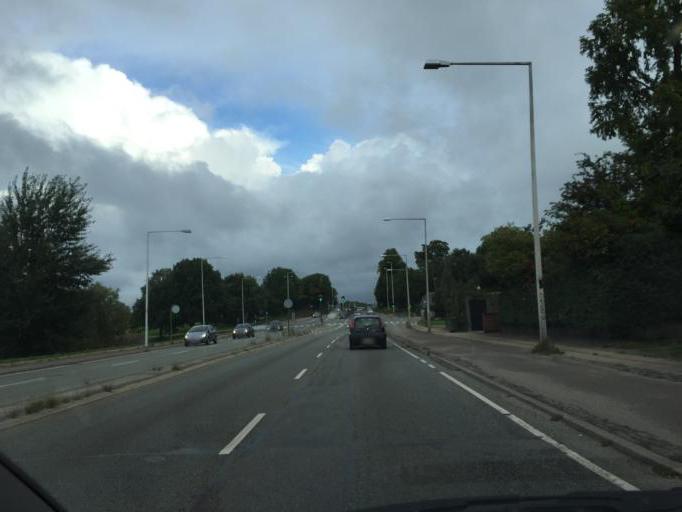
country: DK
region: Capital Region
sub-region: Kobenhavn
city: Vanlose
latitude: 55.7118
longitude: 12.5057
